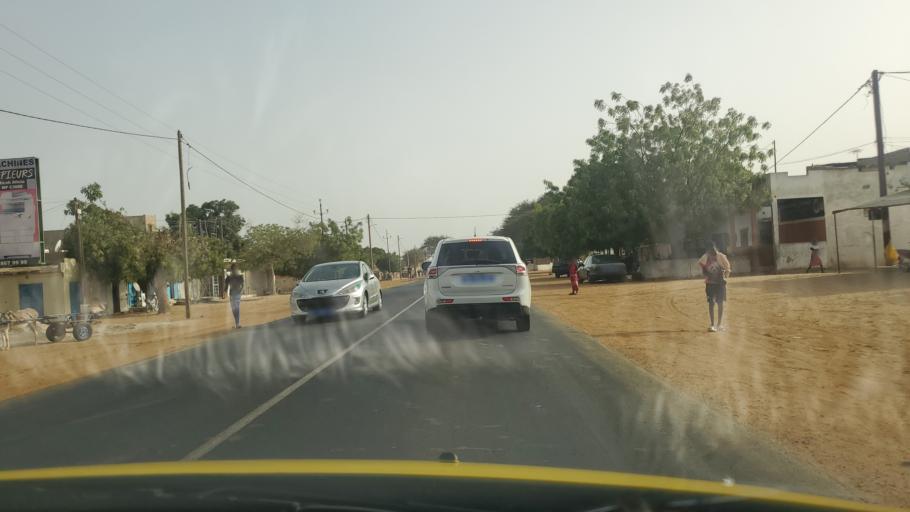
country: SN
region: Thies
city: Mekhe
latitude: 15.2826
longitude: -16.5275
